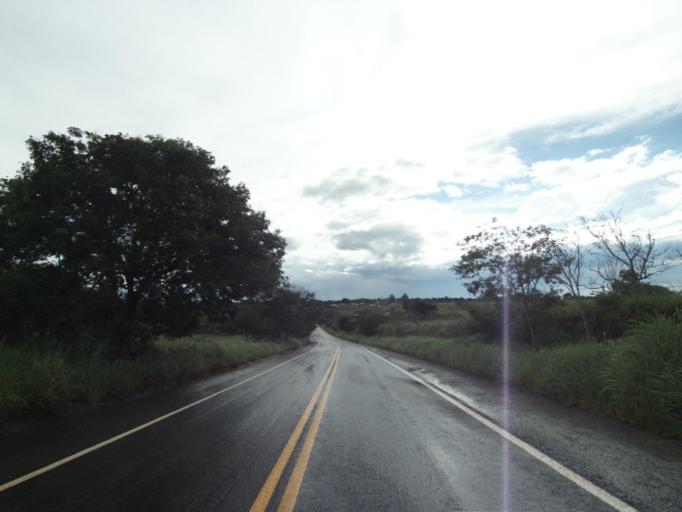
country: BR
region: Goias
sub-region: Itaberai
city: Itaberai
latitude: -15.9141
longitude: -49.5898
